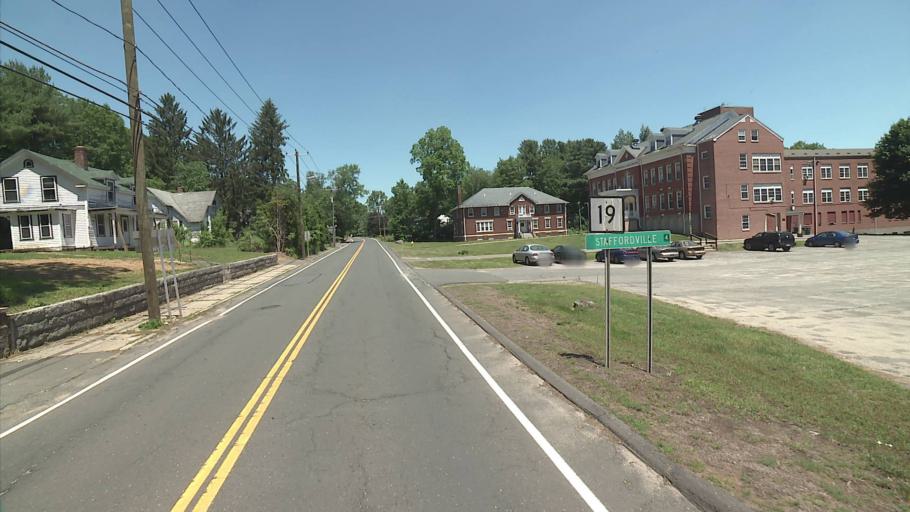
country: US
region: Connecticut
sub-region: Tolland County
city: Stafford Springs
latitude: 41.9564
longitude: -72.2970
